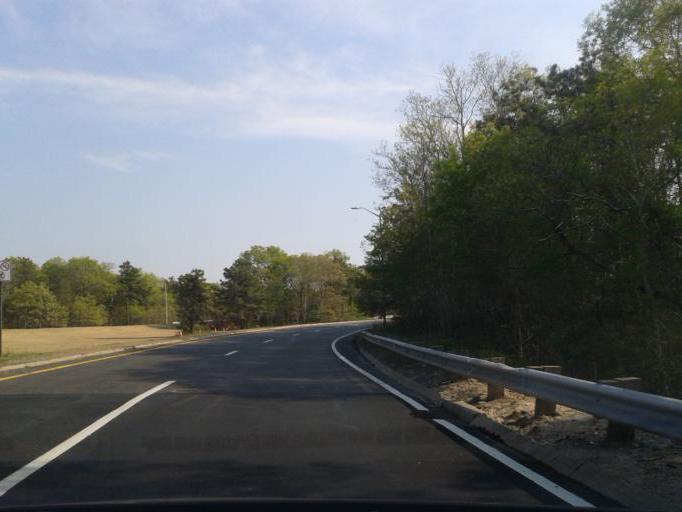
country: US
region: Massachusetts
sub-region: Barnstable County
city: Pocasset
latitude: 41.6845
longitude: -70.5927
